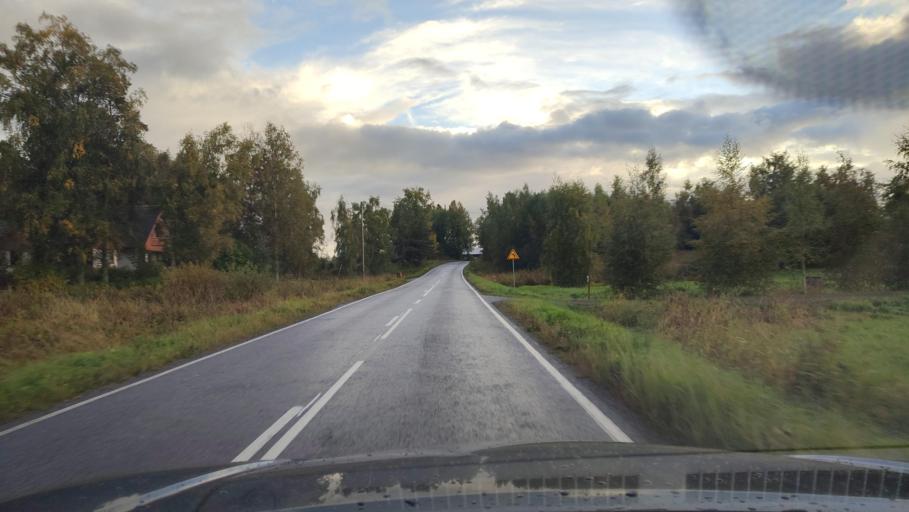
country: FI
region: Ostrobothnia
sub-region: Sydosterbotten
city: Kristinestad
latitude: 62.2859
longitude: 21.4214
